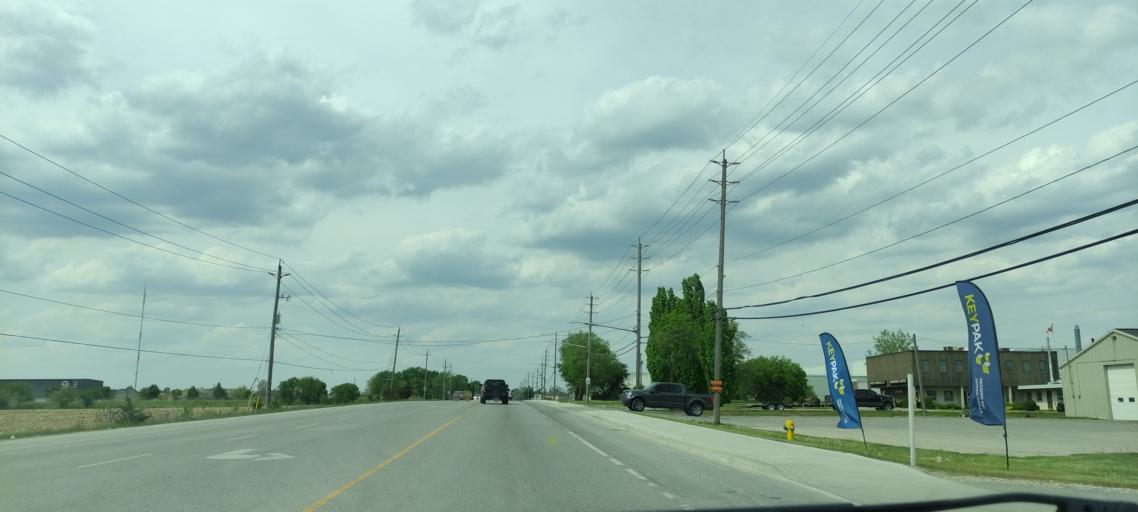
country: CA
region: Ontario
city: London
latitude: 42.9323
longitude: -81.2499
